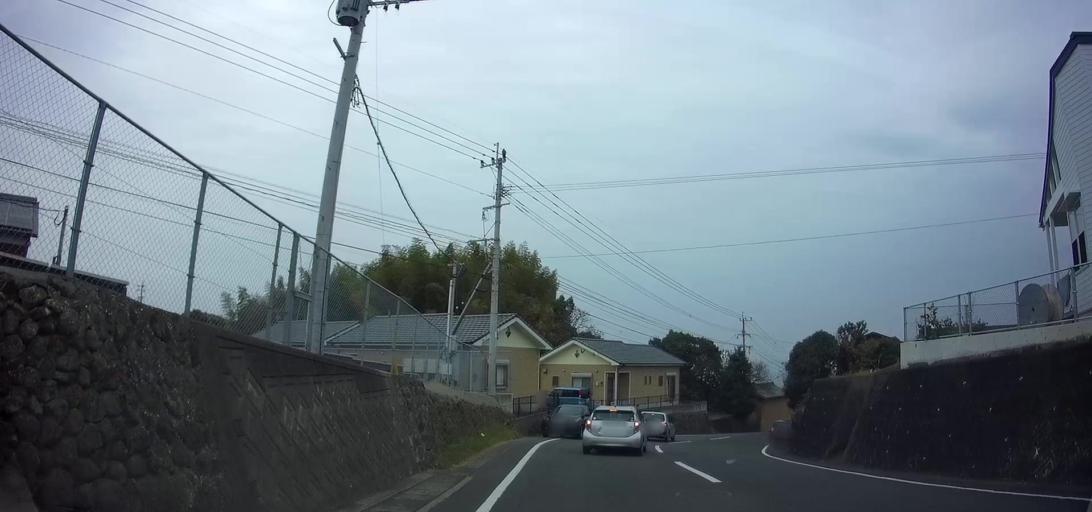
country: JP
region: Nagasaki
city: Shimabara
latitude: 32.6619
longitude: 130.2880
